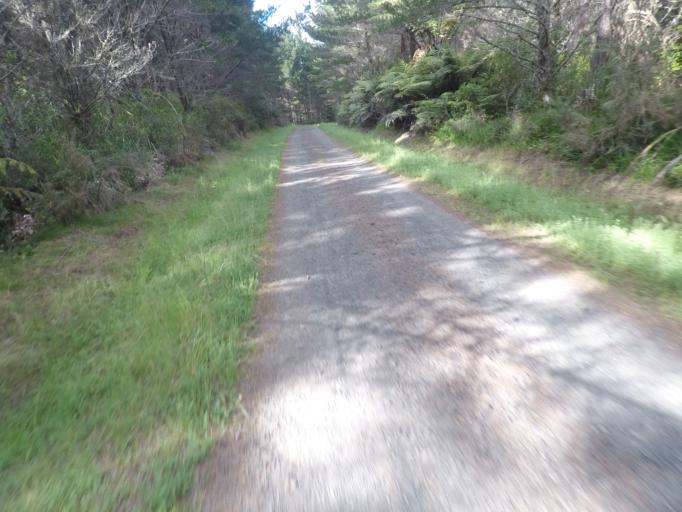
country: NZ
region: Auckland
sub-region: Auckland
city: Muriwai Beach
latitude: -36.7452
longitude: 174.5652
